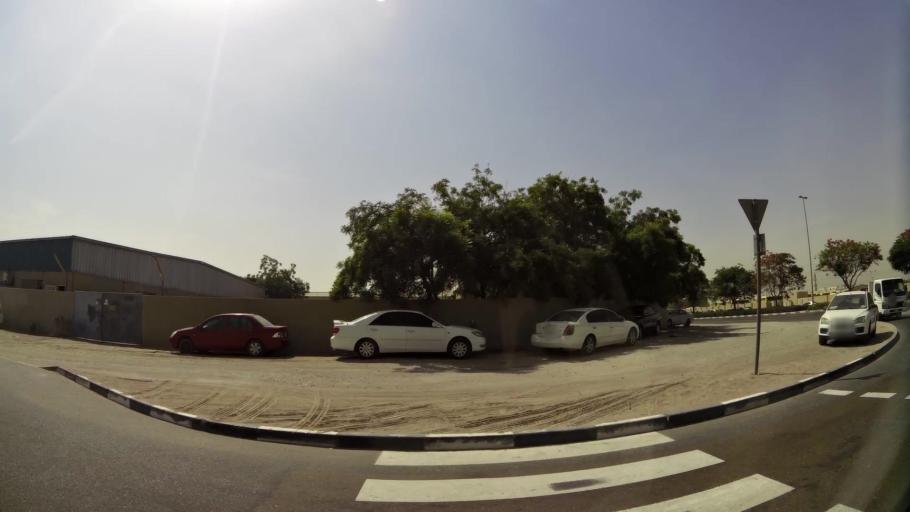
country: AE
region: Ash Shariqah
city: Sharjah
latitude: 25.2769
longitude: 55.3869
